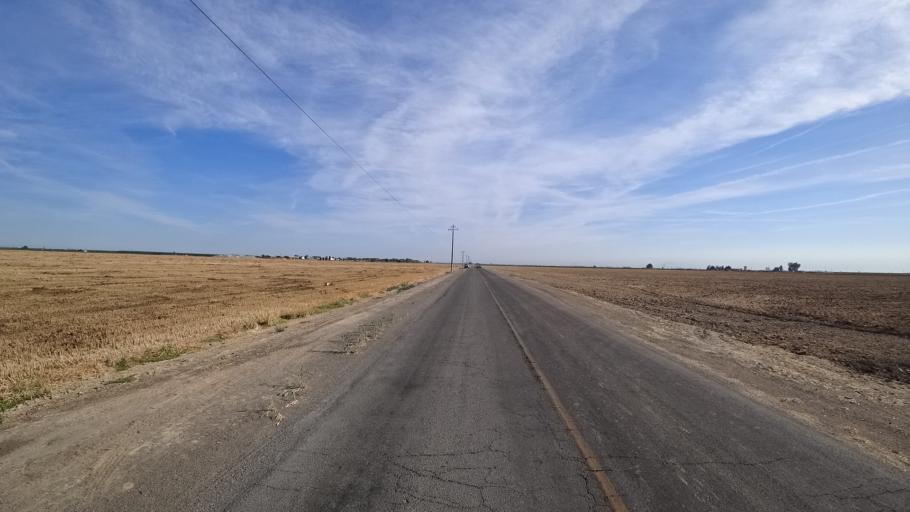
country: US
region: California
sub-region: Tulare County
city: London
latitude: 36.4017
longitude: -119.5288
